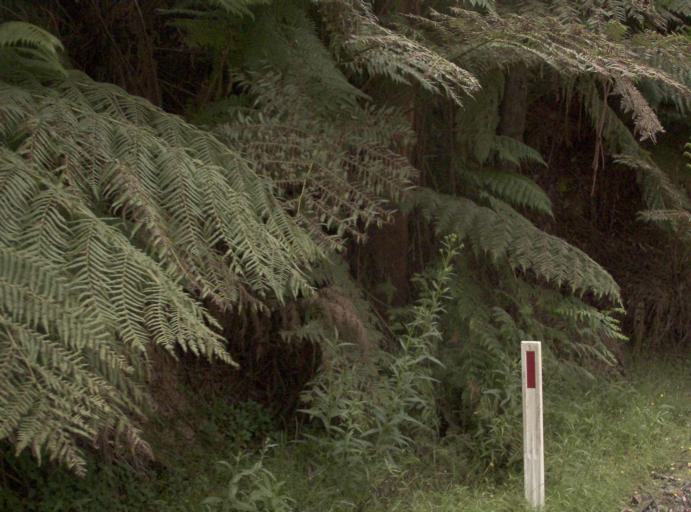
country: AU
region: Victoria
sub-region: Latrobe
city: Traralgon
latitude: -38.4459
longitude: 146.5362
